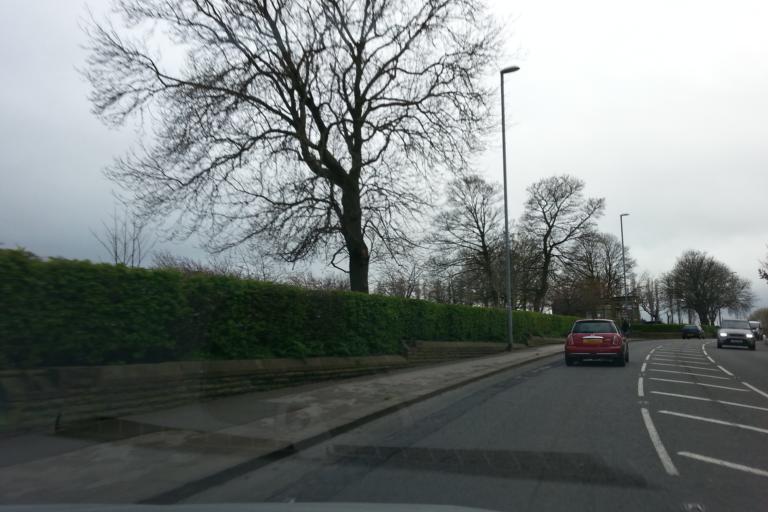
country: GB
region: England
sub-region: City and Borough of Leeds
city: Morley
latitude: 53.7466
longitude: -1.6146
